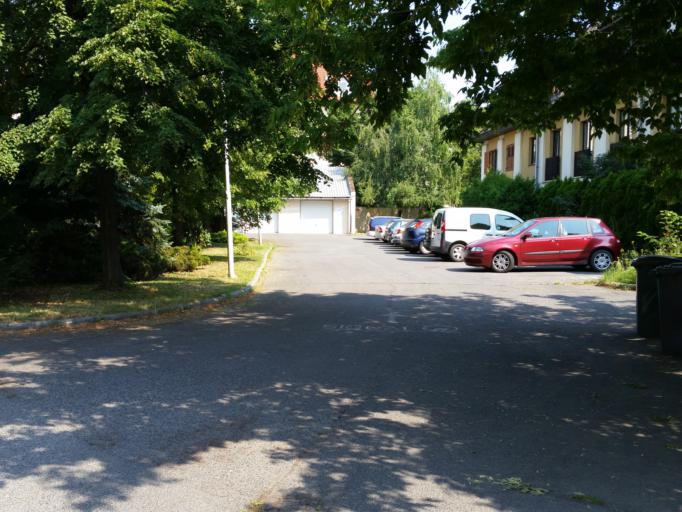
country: HU
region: Vas
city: Szombathely
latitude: 47.2367
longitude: 16.6255
